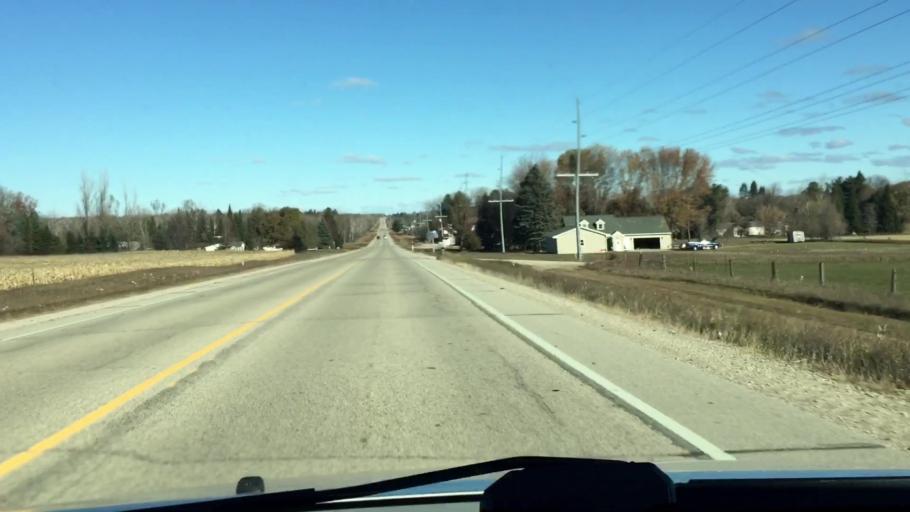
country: US
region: Wisconsin
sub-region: Oconto County
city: Gillett
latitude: 44.8716
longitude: -88.2474
